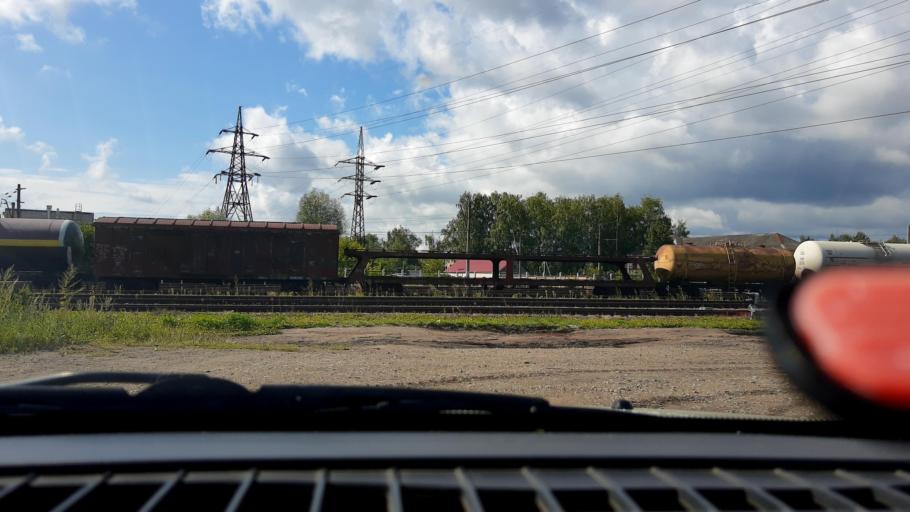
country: RU
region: Nizjnij Novgorod
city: Nizhniy Novgorod
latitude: 56.3089
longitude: 43.8806
